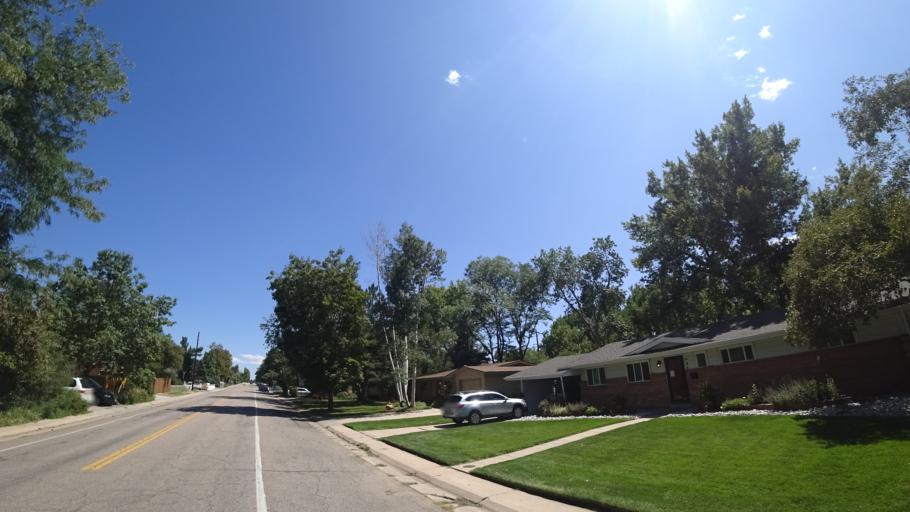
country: US
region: Colorado
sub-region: Arapahoe County
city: Littleton
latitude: 39.6100
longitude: -104.9993
